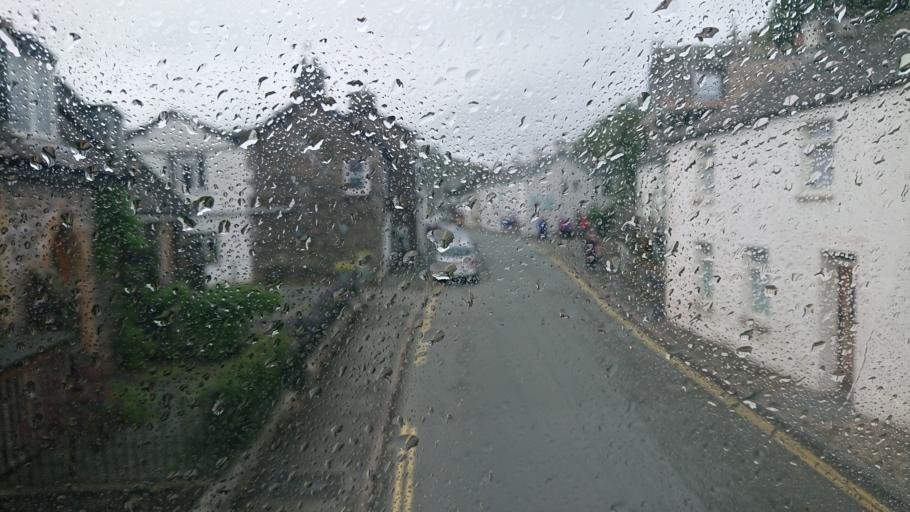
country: GB
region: England
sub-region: Cumbria
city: Kendal
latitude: 54.3759
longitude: -2.8152
